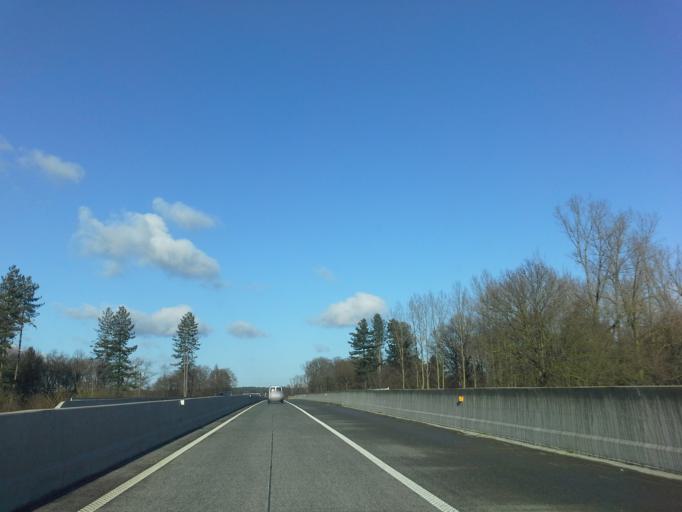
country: BE
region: Flanders
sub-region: Provincie Antwerpen
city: Kasterlee
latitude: 51.2147
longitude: 4.9670
